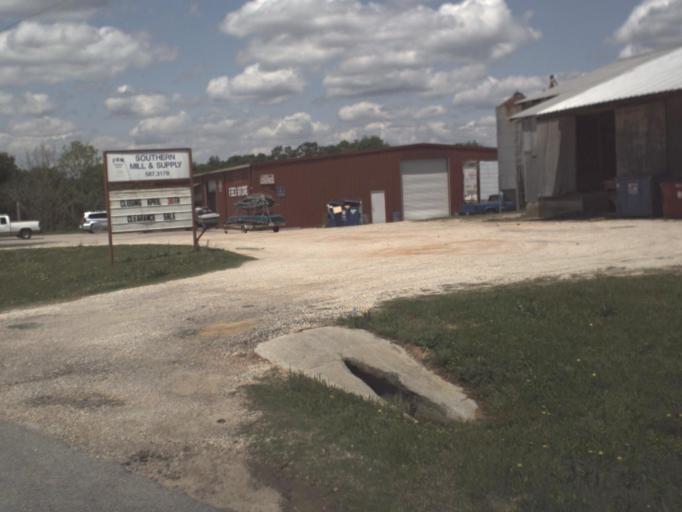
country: US
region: Florida
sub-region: Escambia County
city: Molino
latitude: 30.7503
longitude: -87.3747
